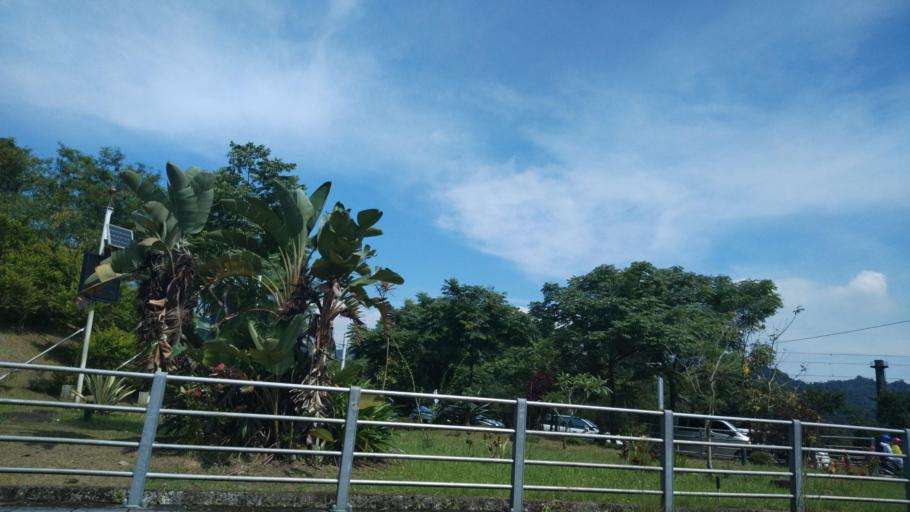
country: TW
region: Taipei
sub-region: Taipei
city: Banqiao
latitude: 24.9543
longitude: 121.5093
